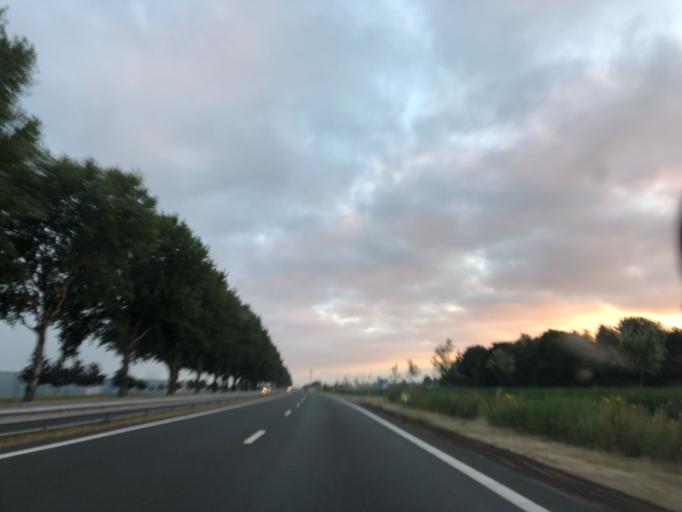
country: NL
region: Groningen
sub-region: Gemeente Veendam
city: Veendam
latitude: 53.1247
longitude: 6.8996
